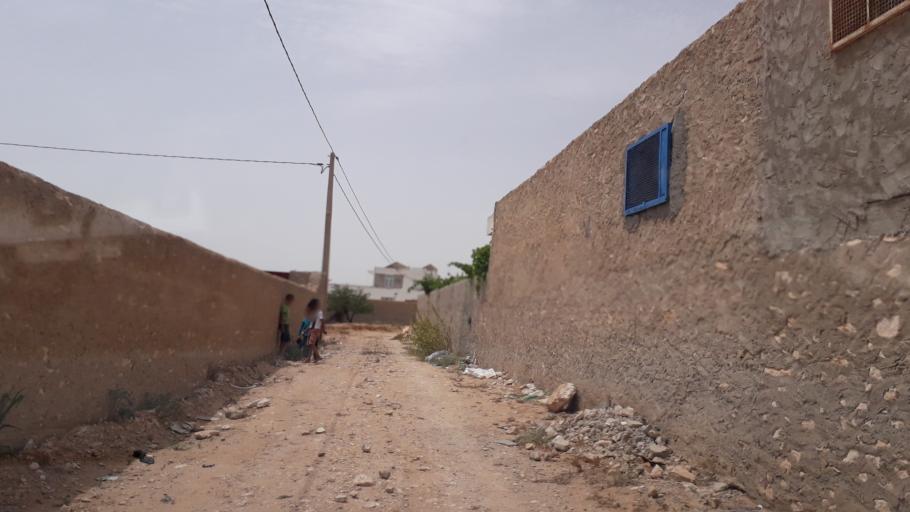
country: TN
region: Safaqis
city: Al Qarmadah
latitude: 34.8512
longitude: 10.7656
